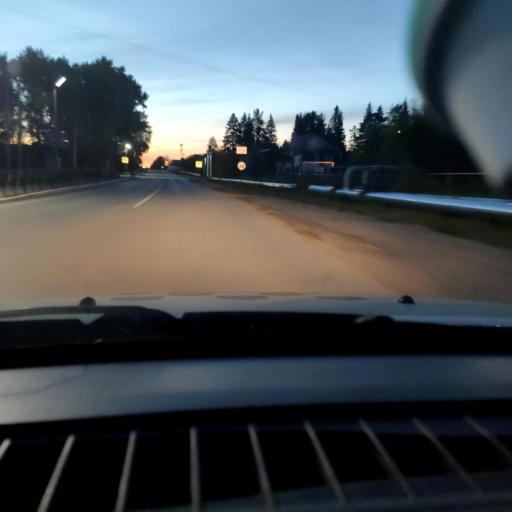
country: RU
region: Perm
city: Polazna
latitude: 58.2912
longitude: 56.3976
